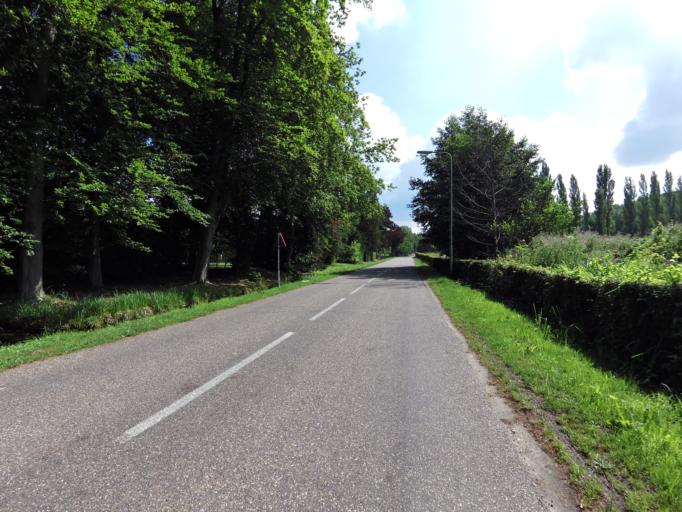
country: NL
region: Limburg
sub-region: Valkenburg aan de Geul
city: Schin op Geul
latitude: 50.8293
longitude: 5.8894
